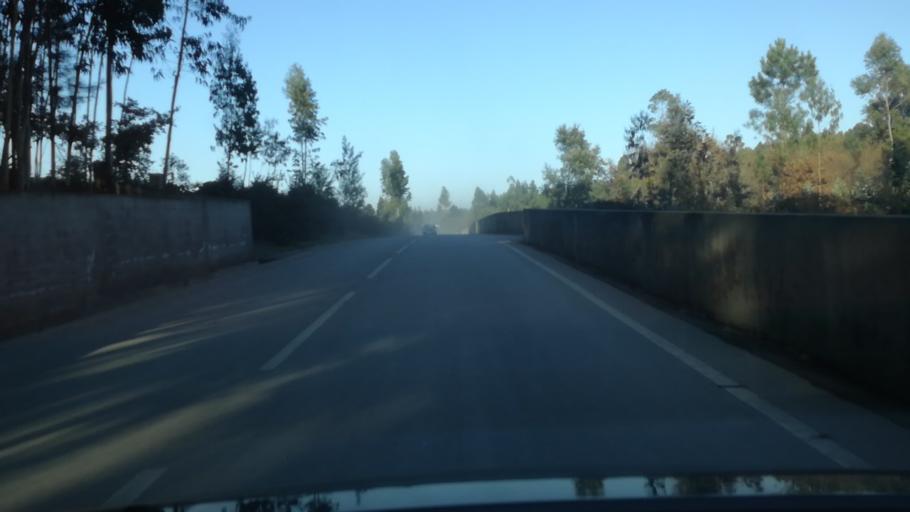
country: PT
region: Braga
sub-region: Vila Nova de Famalicao
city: Ferreiros
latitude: 41.3606
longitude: -8.5371
